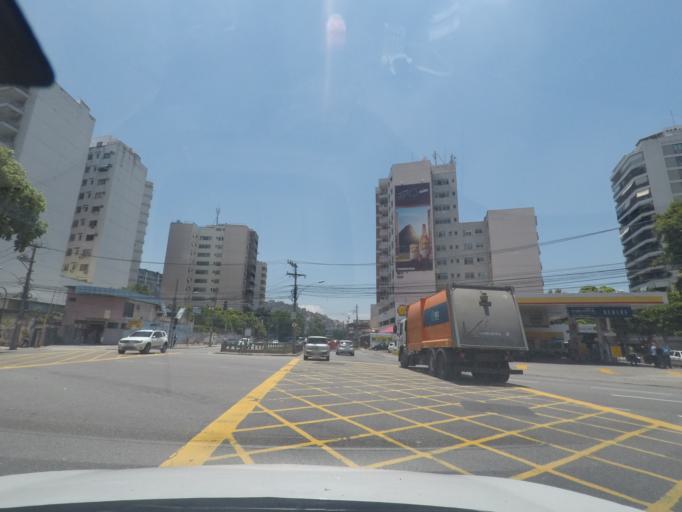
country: BR
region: Rio de Janeiro
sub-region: Rio De Janeiro
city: Rio de Janeiro
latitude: -22.9140
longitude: -43.2340
